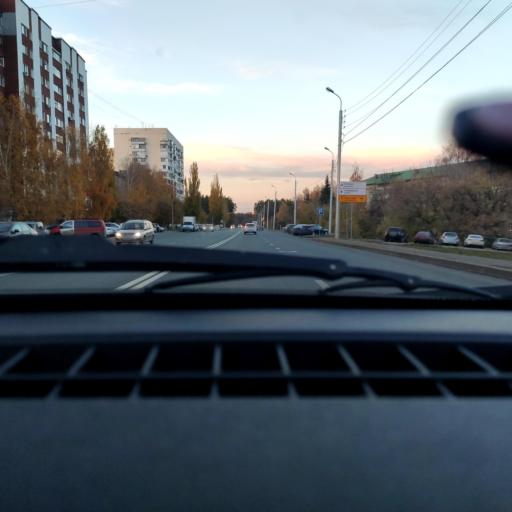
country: RU
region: Bashkortostan
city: Ufa
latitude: 54.7916
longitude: 56.0420
